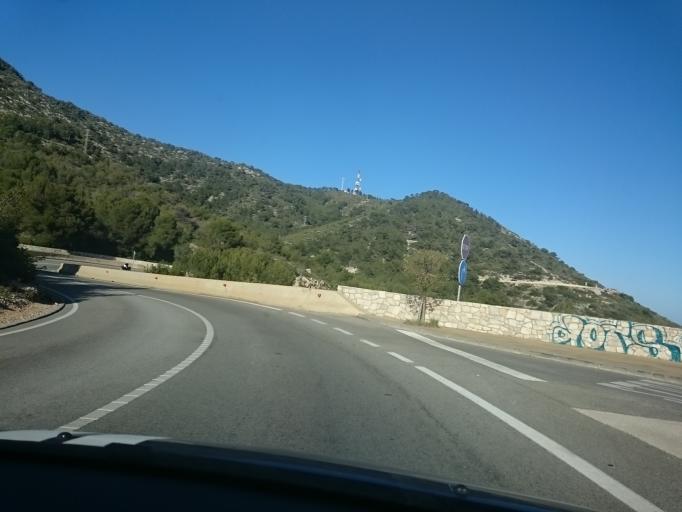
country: ES
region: Catalonia
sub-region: Provincia de Barcelona
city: Sitges
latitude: 41.2358
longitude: 1.8399
